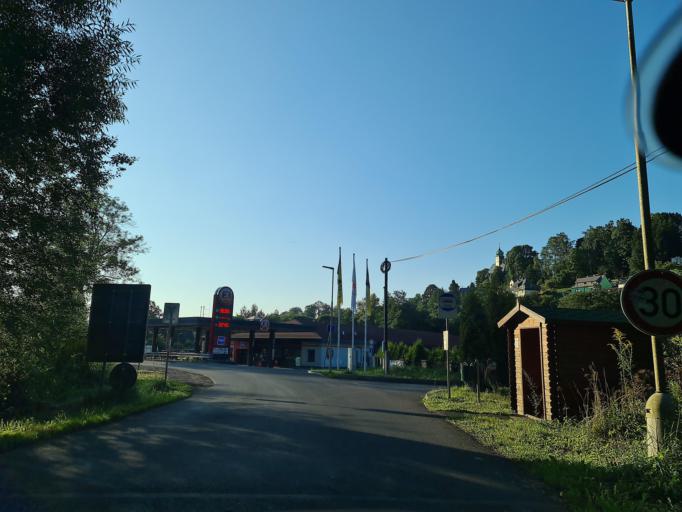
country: DE
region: Saxony
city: Olbernhau
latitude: 50.6495
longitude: 13.3728
